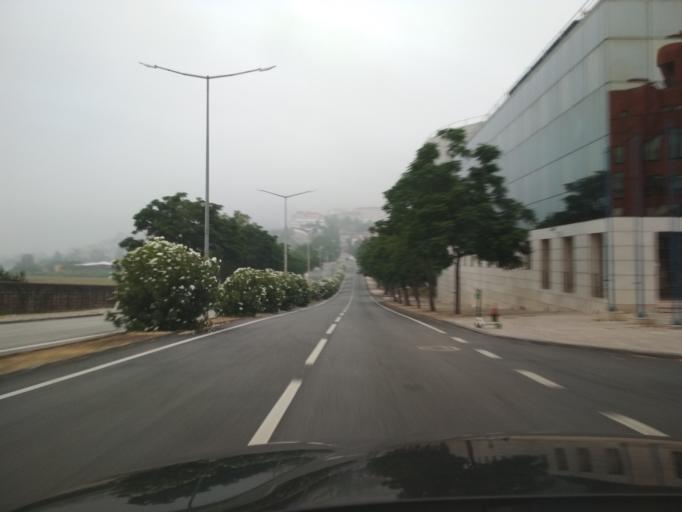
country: PT
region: Coimbra
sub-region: Coimbra
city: Coimbra
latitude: 40.1949
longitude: -8.4208
